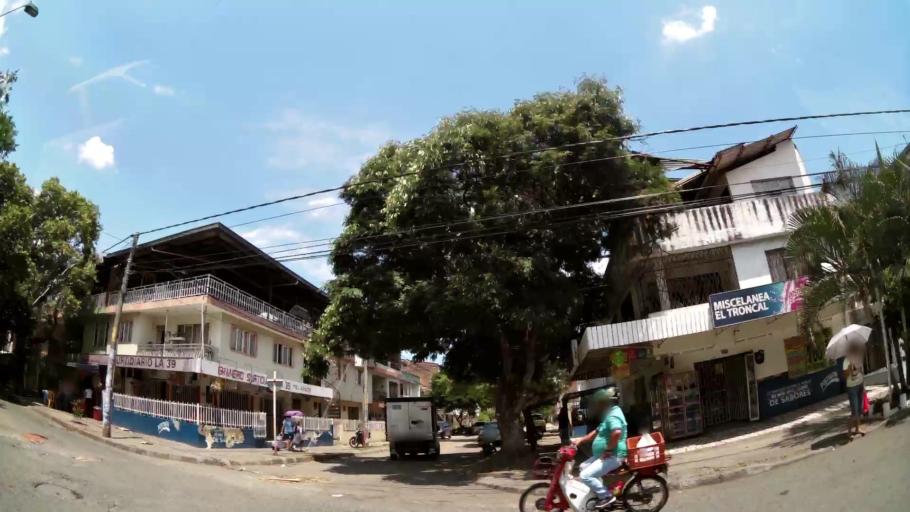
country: CO
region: Valle del Cauca
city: Cali
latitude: 3.4488
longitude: -76.5069
